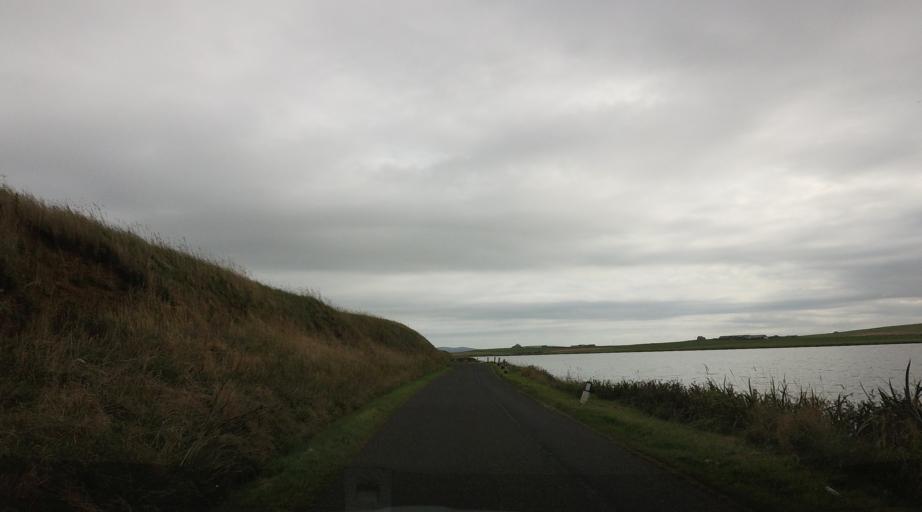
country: GB
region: Scotland
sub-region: Orkney Islands
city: Stromness
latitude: 59.0461
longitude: -3.3205
